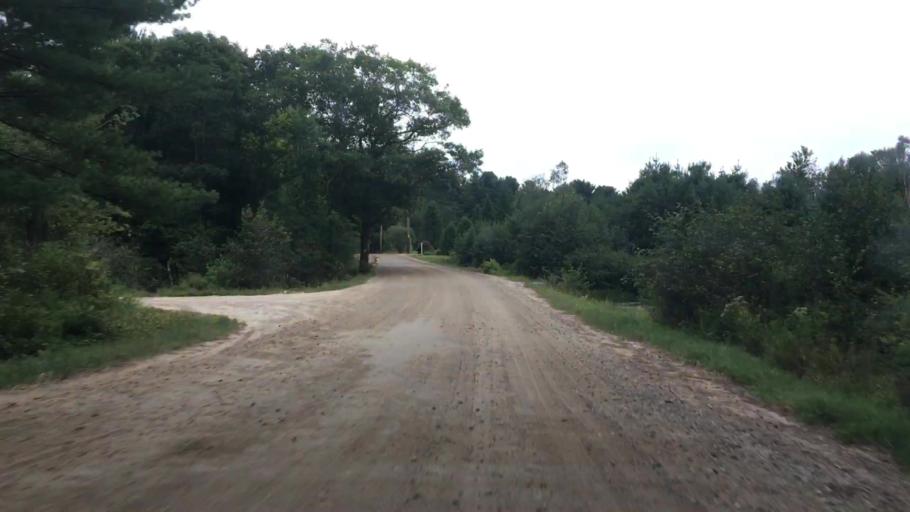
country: US
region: Maine
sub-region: Cumberland County
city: New Gloucester
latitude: 43.9084
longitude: -70.2384
